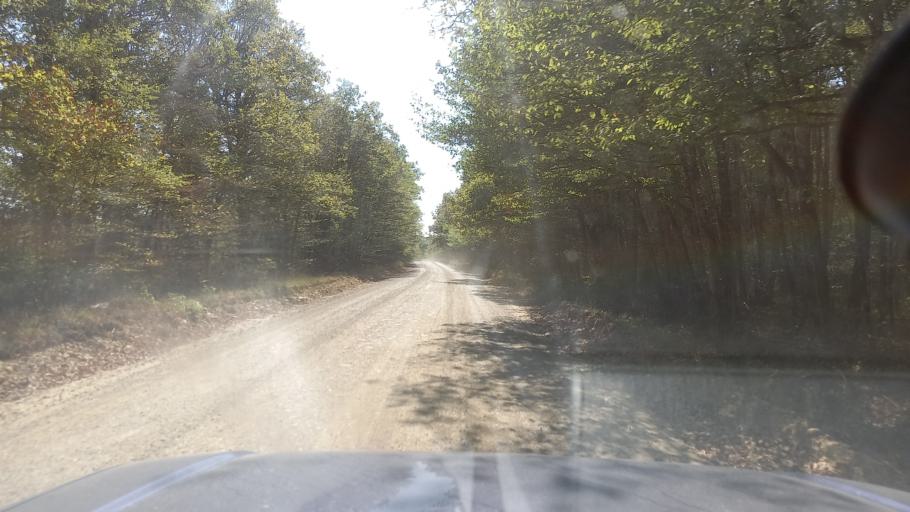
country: RU
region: Krasnodarskiy
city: Azovskaya
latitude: 44.6812
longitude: 38.6347
